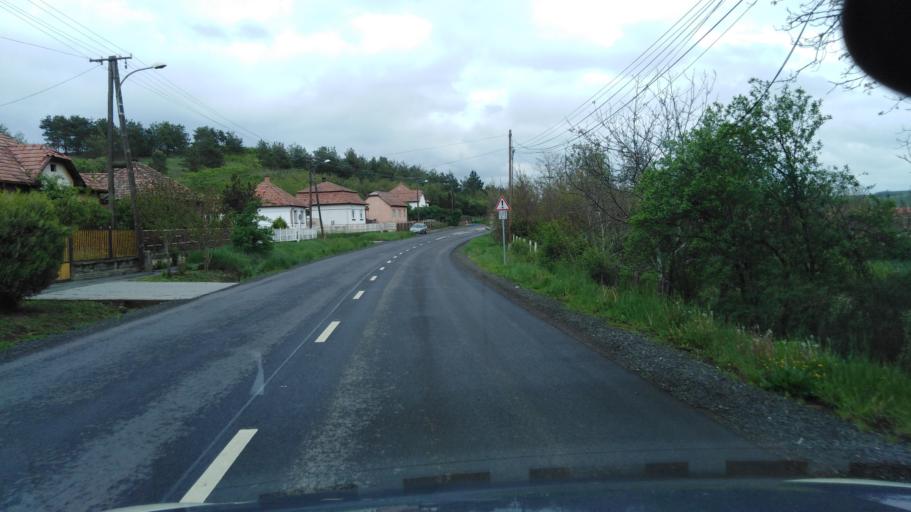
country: HU
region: Nograd
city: Szecseny
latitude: 48.1276
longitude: 19.5815
